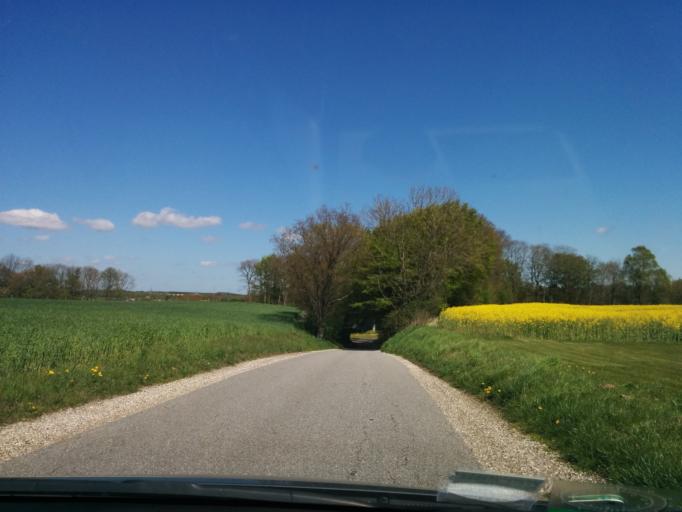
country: DK
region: Central Jutland
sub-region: Randers Kommune
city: Randers
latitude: 56.4137
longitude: 10.0851
